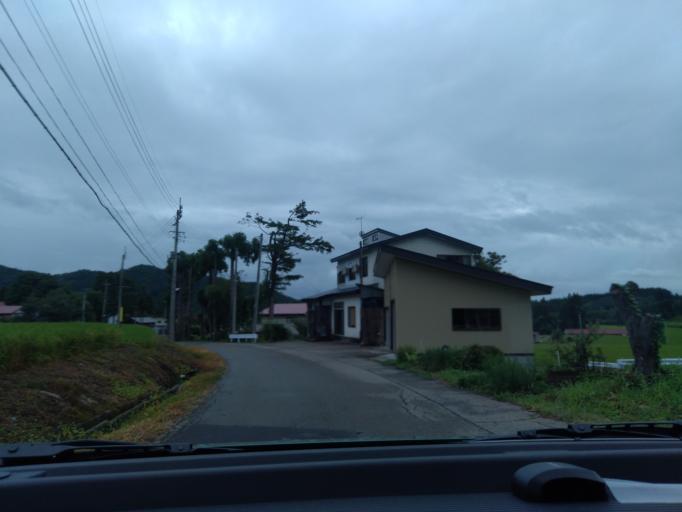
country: JP
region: Akita
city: Yokotemachi
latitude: 39.4255
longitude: 140.6017
